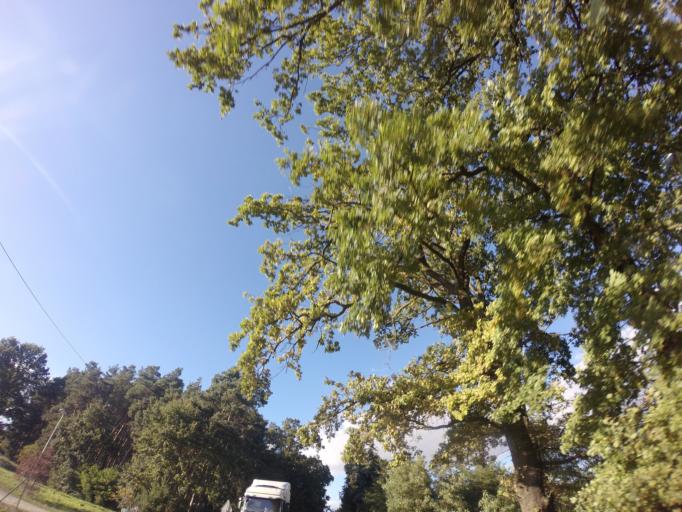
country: PL
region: Greater Poland Voivodeship
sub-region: Powiat nowotomyski
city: Nowy Tomysl
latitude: 52.3463
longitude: 16.1054
